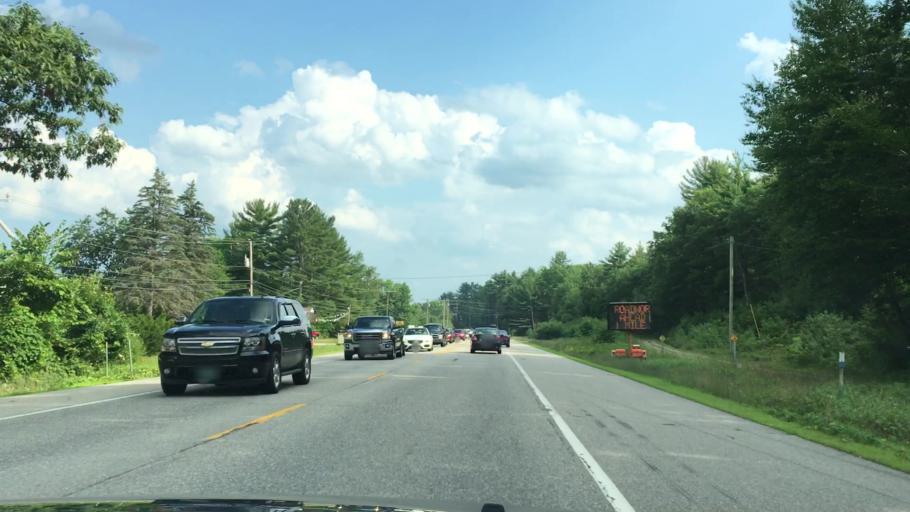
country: US
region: New Hampshire
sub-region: Strafford County
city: Farmington
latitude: 43.3512
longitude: -71.0262
